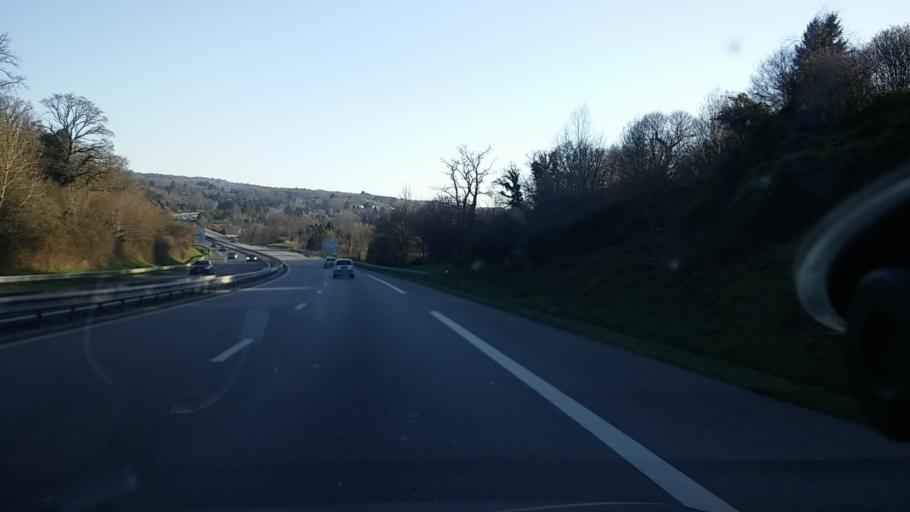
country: FR
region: Limousin
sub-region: Departement de la Haute-Vienne
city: Bessines-sur-Gartempe
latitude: 46.1195
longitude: 1.3756
